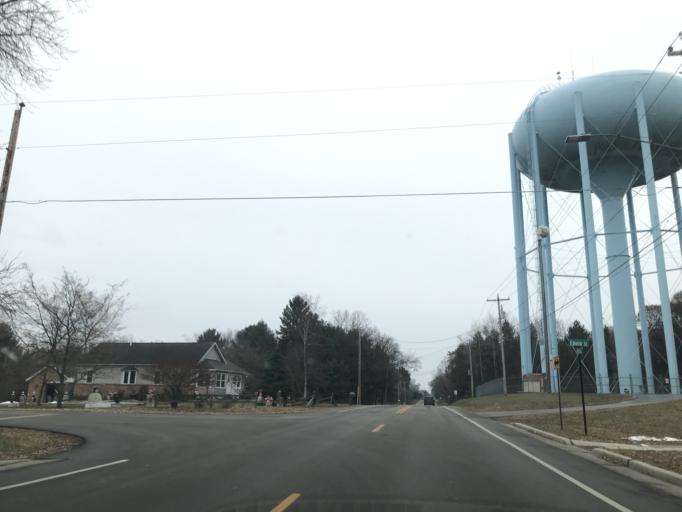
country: US
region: Wisconsin
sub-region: Marinette County
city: Marinette
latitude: 45.0782
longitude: -87.6296
